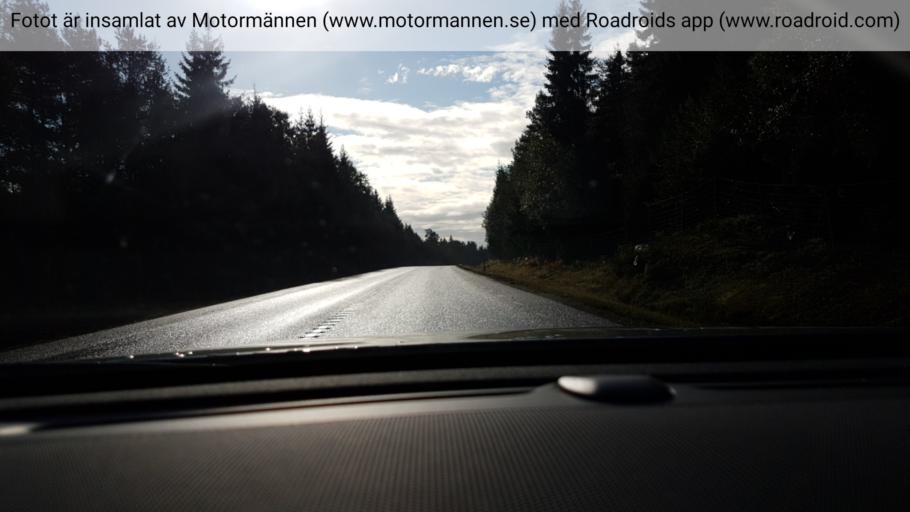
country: SE
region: Vaestra Goetaland
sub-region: Harryda Kommun
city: Hindas
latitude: 57.6688
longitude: 12.3615
